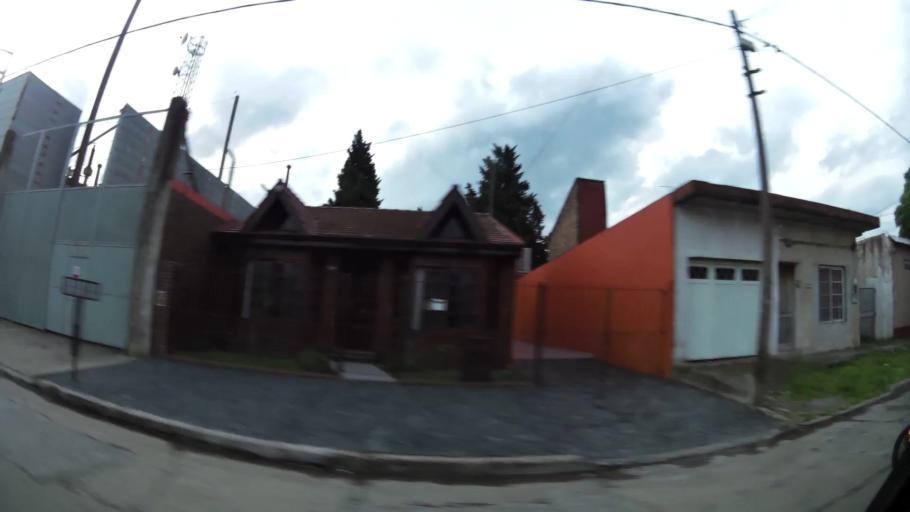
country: AR
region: Buenos Aires
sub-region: Partido de Quilmes
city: Quilmes
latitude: -34.7451
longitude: -58.2334
